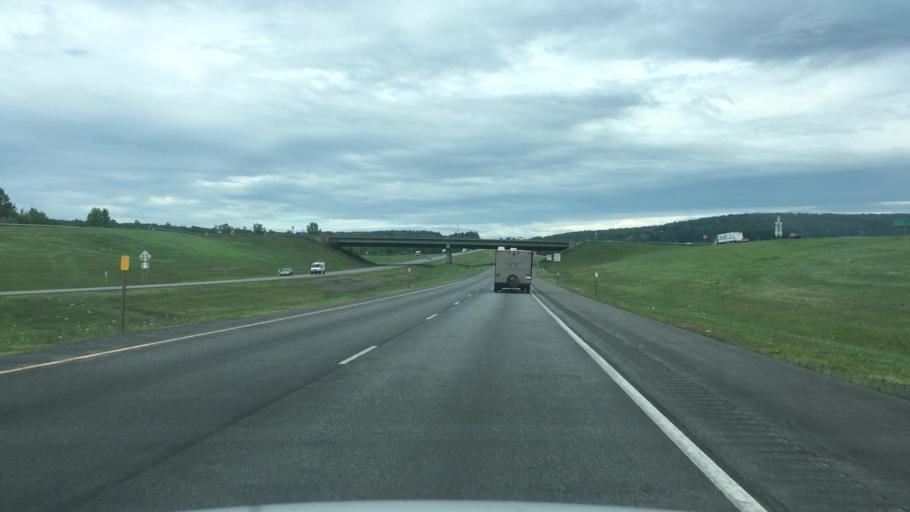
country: US
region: New York
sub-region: Schoharie County
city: Schoharie
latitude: 42.7063
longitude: -74.3174
